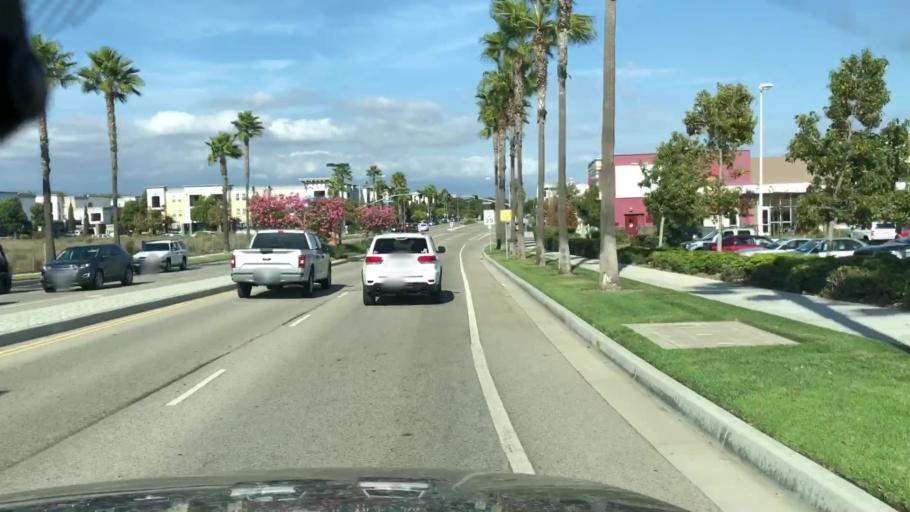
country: US
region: California
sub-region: Ventura County
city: El Rio
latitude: 34.2418
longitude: -119.1799
